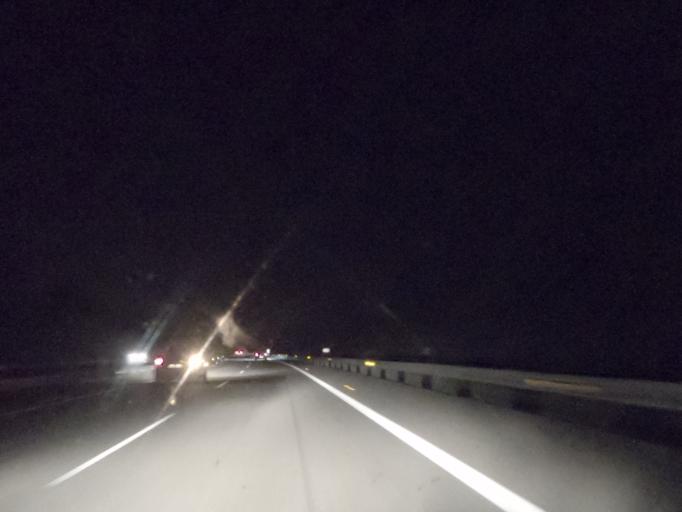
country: ES
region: Galicia
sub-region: Provincia da Coruna
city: Abegondo
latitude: 43.2369
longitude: -8.2588
